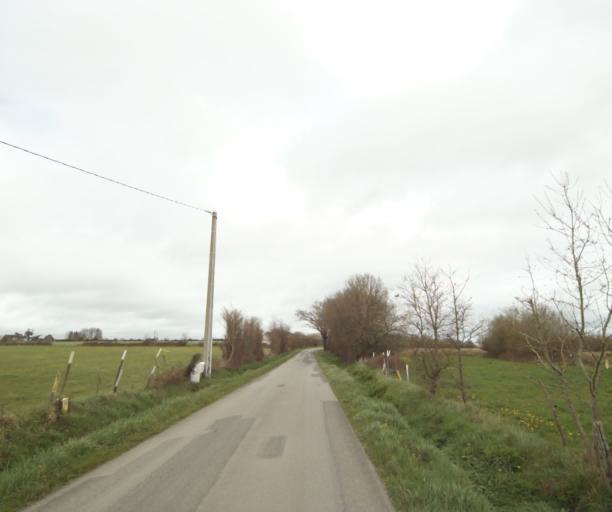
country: FR
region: Pays de la Loire
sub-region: Departement de la Loire-Atlantique
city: Bouvron
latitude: 47.4287
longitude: -1.8980
